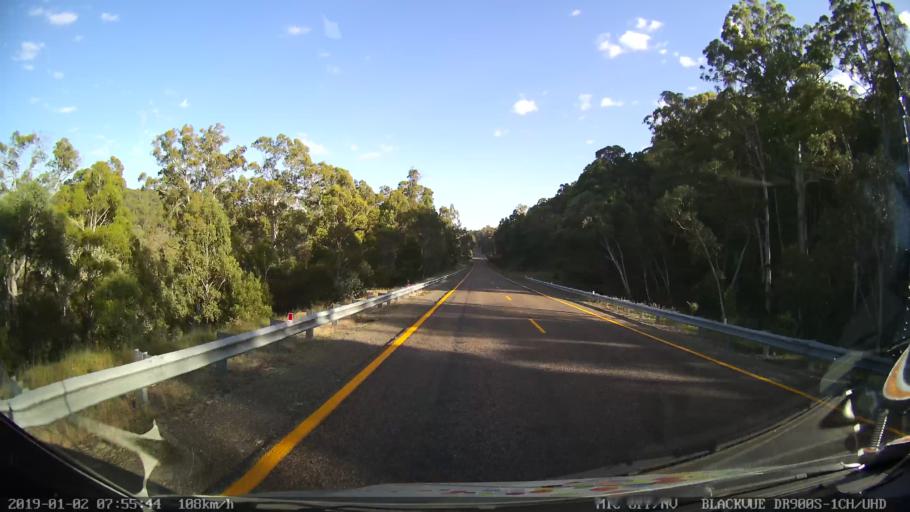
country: AU
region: New South Wales
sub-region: Tumut Shire
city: Tumut
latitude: -35.6802
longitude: 148.4864
